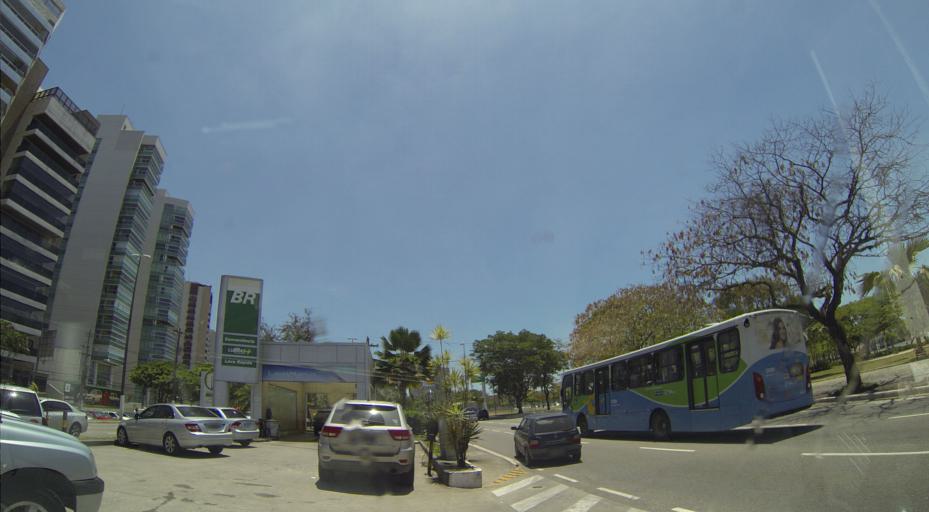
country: BR
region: Espirito Santo
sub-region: Vila Velha
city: Vila Velha
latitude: -20.3033
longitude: -40.2916
